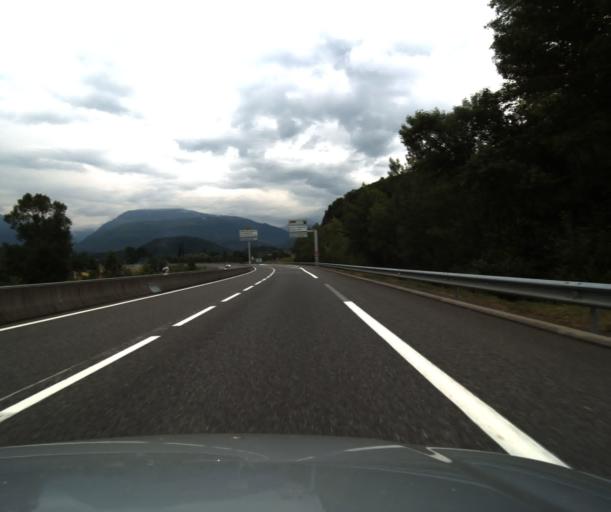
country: FR
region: Midi-Pyrenees
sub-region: Departement des Hautes-Pyrenees
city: Argeles-Gazost
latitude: 43.0429
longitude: -0.0631
